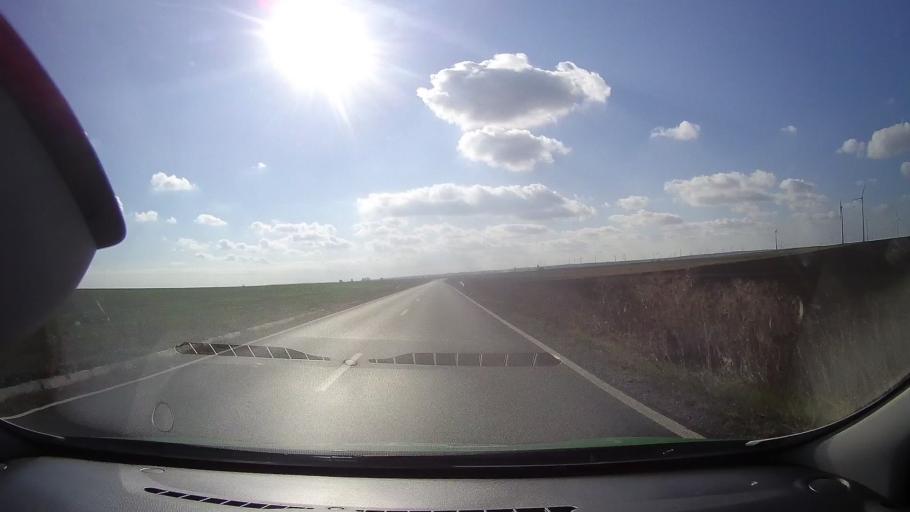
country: RO
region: Constanta
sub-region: Comuna Mihai Viteazu
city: Mihai Viteazu
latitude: 44.6705
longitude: 28.6836
